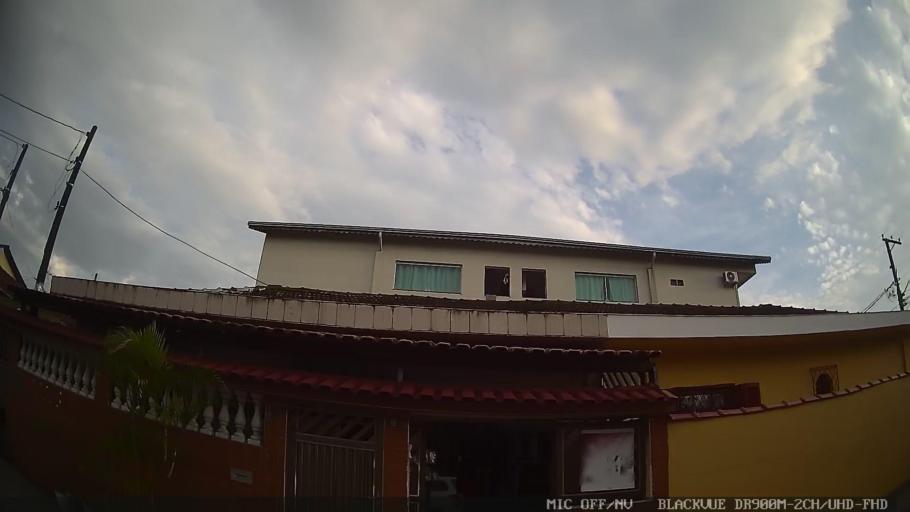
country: BR
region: Sao Paulo
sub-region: Cubatao
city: Cubatao
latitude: -23.8940
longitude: -46.4248
